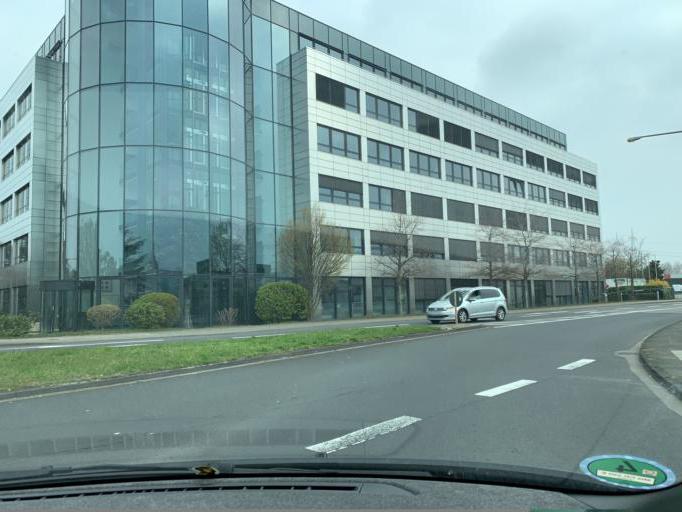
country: DE
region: North Rhine-Westphalia
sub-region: Regierungsbezirk Koln
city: Leverkusen
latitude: 51.0347
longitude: 6.9231
